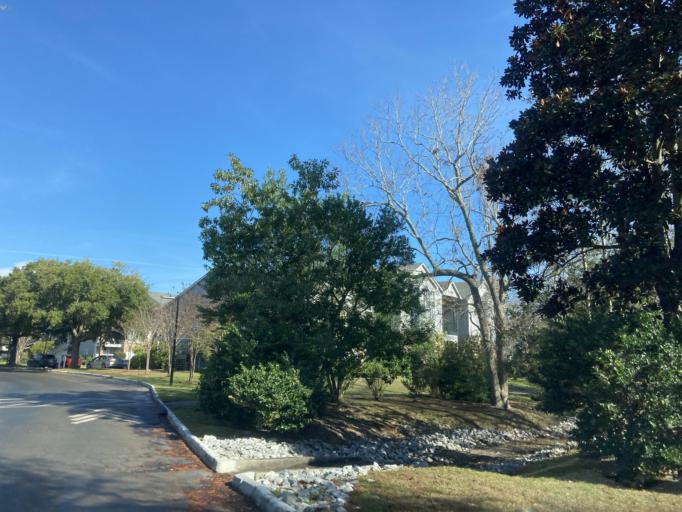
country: US
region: Mississippi
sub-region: Harrison County
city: West Gulfport
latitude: 30.3983
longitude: -89.0234
